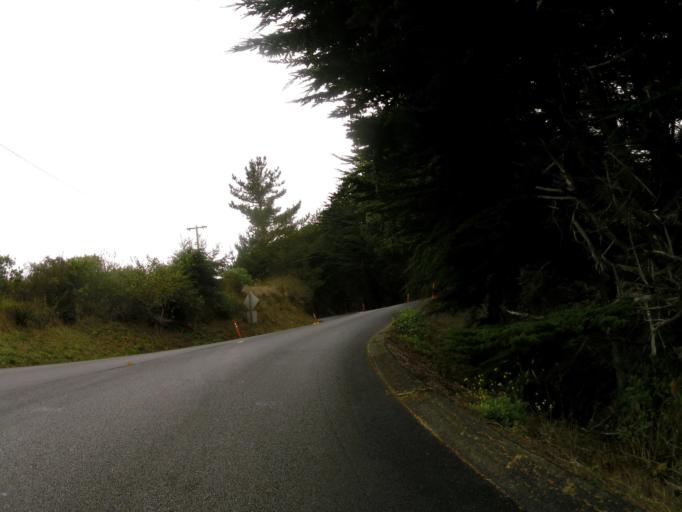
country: US
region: California
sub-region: Sonoma County
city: Monte Rio
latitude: 38.4321
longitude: -123.1066
